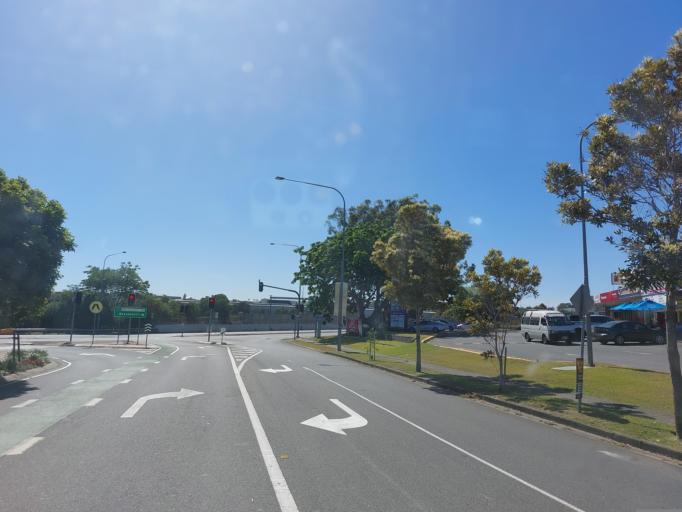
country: AU
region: Queensland
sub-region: Brisbane
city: Sunnybank
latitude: -27.5894
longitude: 153.0271
